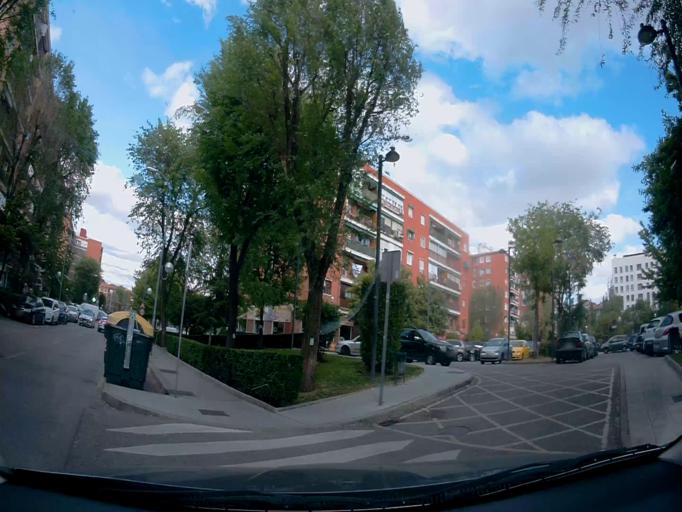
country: ES
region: Madrid
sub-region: Provincia de Madrid
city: Mostoles
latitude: 40.3160
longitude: -3.8755
